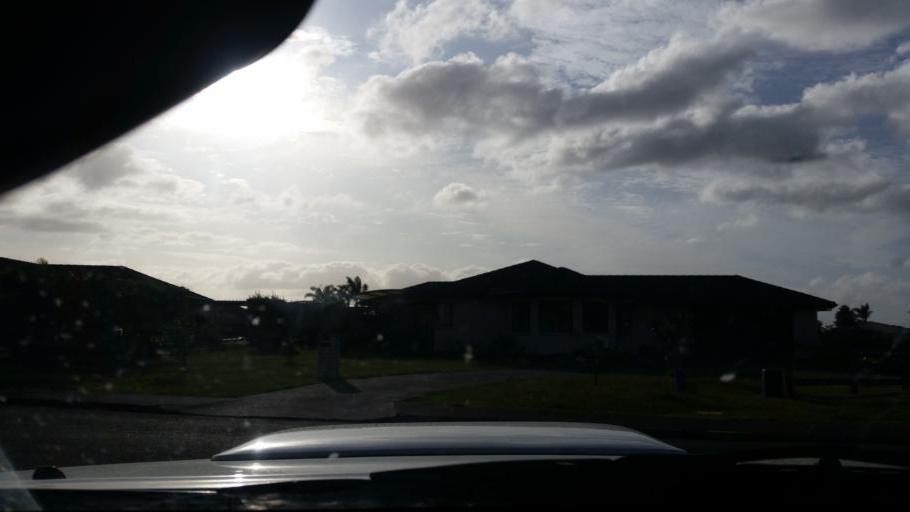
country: NZ
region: Northland
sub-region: Kaipara District
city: Dargaville
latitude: -35.9279
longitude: 173.8646
